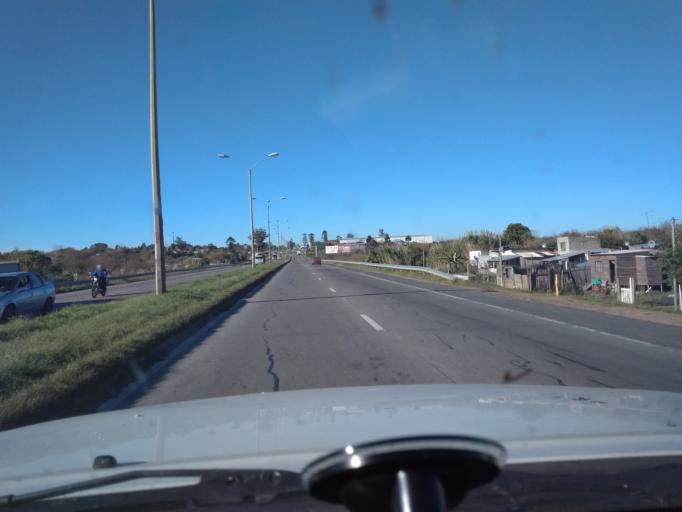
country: UY
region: Canelones
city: Colonia Nicolich
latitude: -34.7744
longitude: -56.0346
